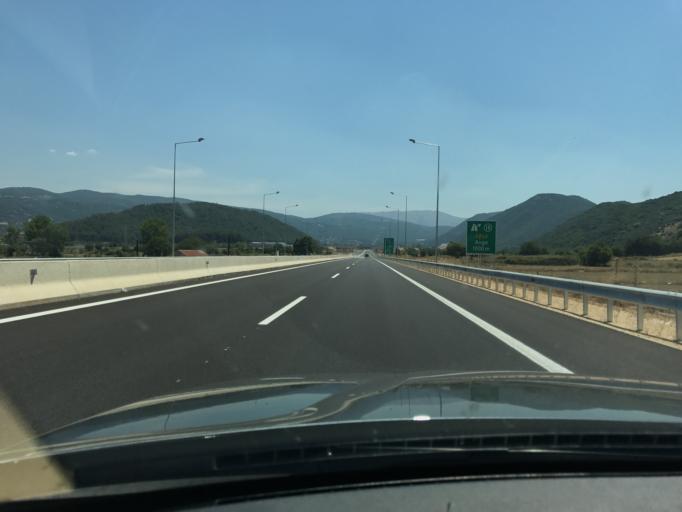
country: GR
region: Epirus
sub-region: Nomos Ioanninon
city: Agia Kyriaki
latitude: 39.5394
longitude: 20.8653
